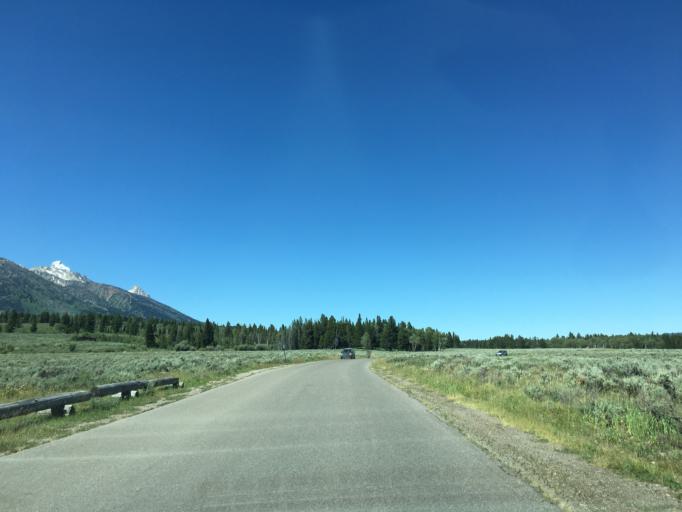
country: US
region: Wyoming
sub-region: Teton County
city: Moose Wilson Road
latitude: 43.6000
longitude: -110.7977
